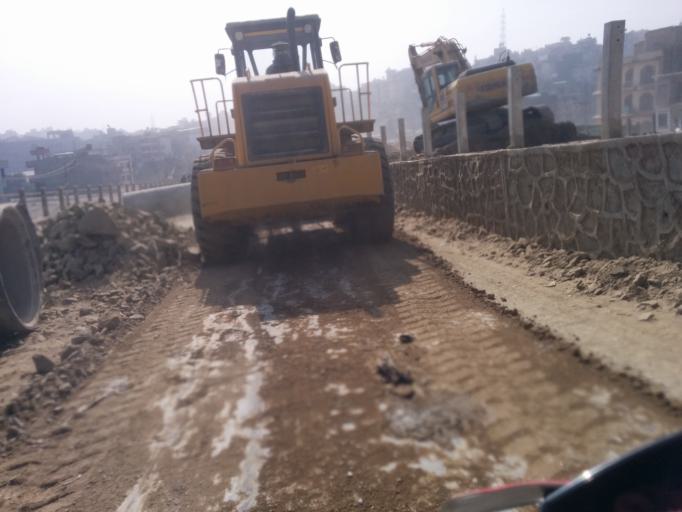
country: NP
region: Central Region
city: Kirtipur
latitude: 27.6913
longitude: 85.2829
